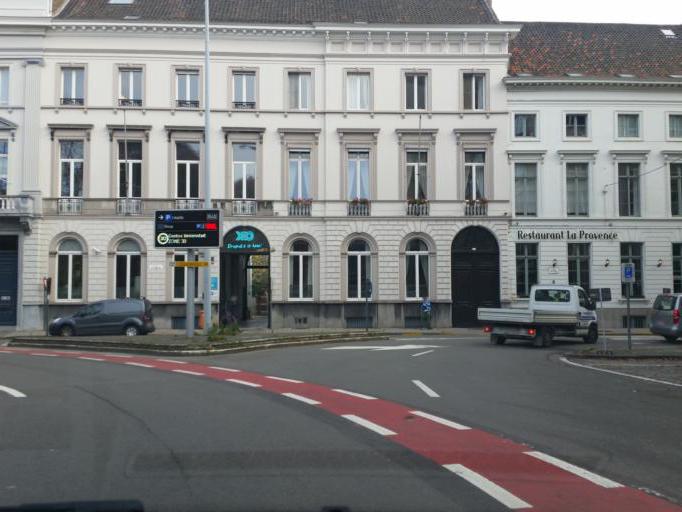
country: BE
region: Flanders
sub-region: Provincie Oost-Vlaanderen
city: Ledeberg
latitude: 51.0493
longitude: 3.7350
